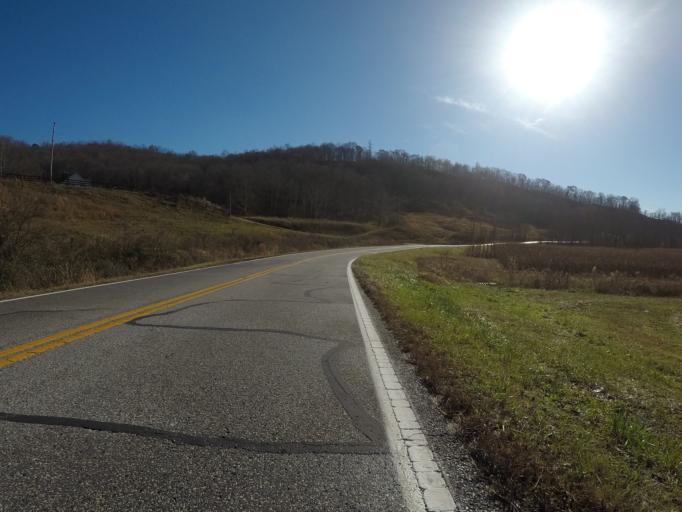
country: US
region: West Virginia
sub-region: Cabell County
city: Huntington
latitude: 38.4774
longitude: -82.4444
